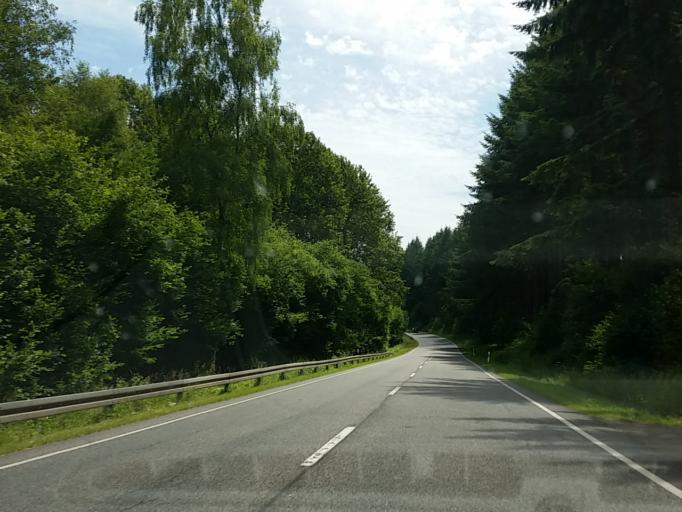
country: DE
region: Saarland
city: Britten
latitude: 49.5237
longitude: 6.7104
